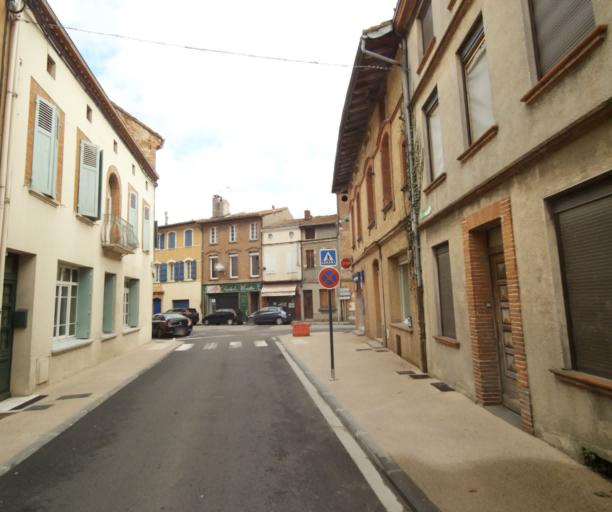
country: FR
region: Midi-Pyrenees
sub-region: Departement de l'Ariege
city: Saverdun
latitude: 43.2331
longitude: 1.5753
